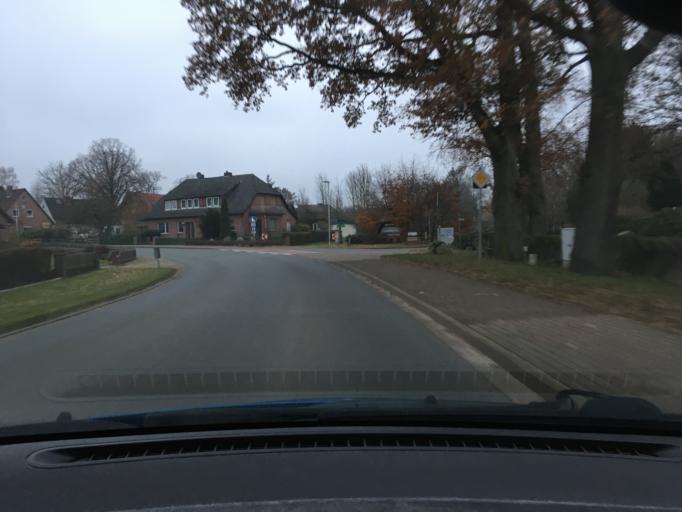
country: DE
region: Lower Saxony
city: Bispingen
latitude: 53.1111
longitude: 9.9629
